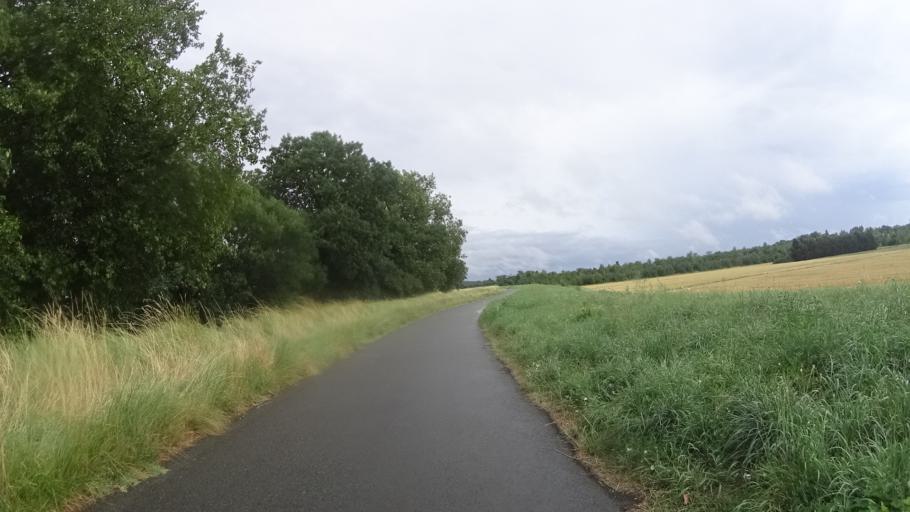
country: FR
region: Centre
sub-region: Departement du Loiret
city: Saint-Jean-de-Braye
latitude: 47.8924
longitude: 1.9751
